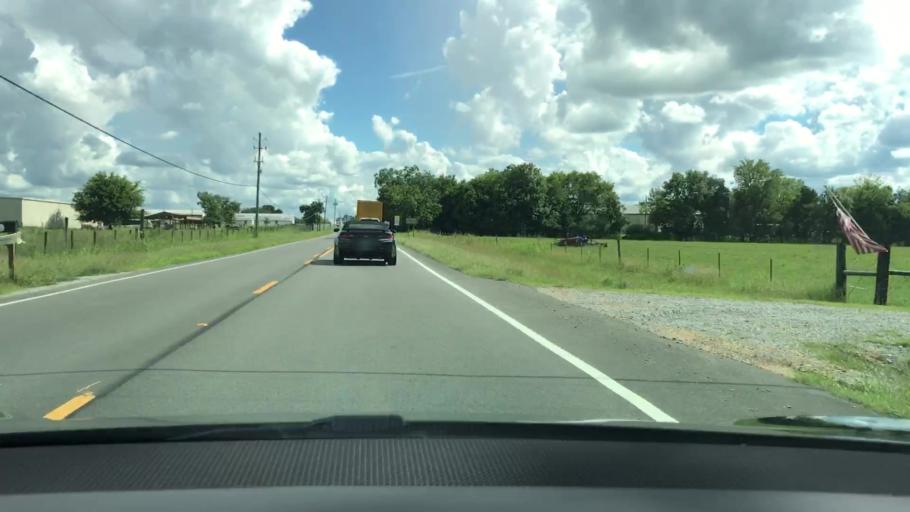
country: US
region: Alabama
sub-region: Montgomery County
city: Pike Road
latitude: 32.2883
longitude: -86.1026
